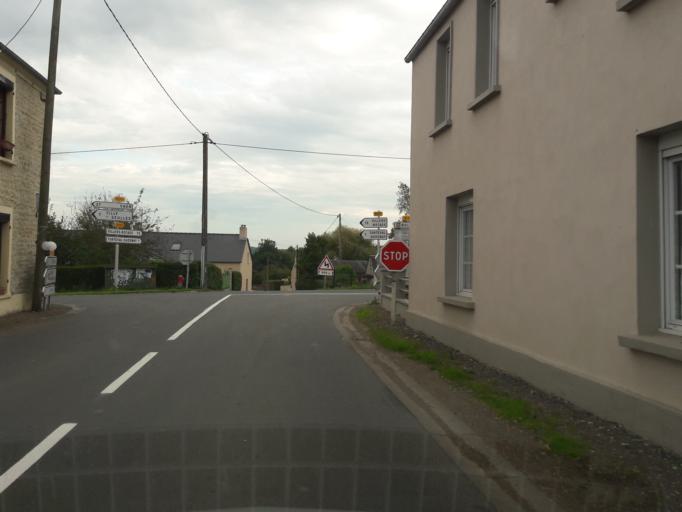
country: FR
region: Lower Normandy
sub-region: Departement du Calvados
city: Bayeux
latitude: 49.1824
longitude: -0.7235
